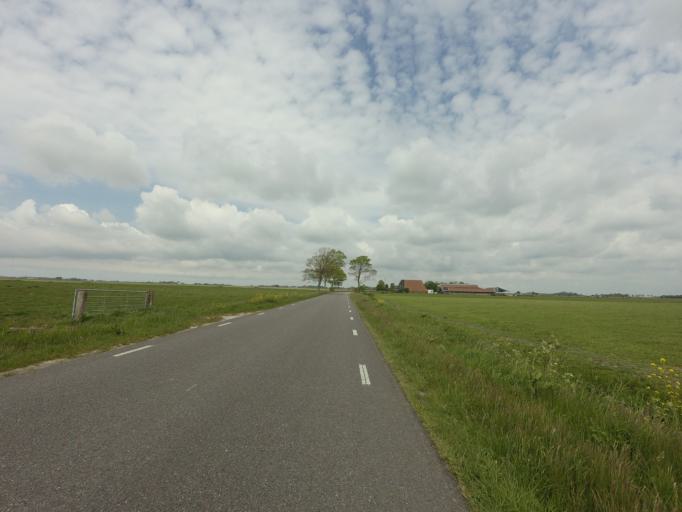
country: NL
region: Friesland
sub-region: Sudwest Fryslan
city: Bolsward
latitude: 53.0960
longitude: 5.5345
